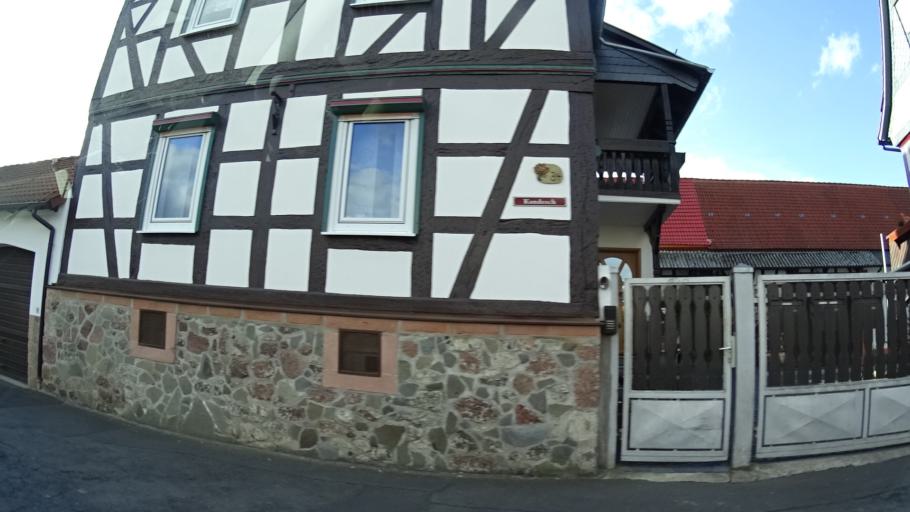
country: DE
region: Hesse
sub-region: Regierungsbezirk Darmstadt
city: Glauburg
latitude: 50.3154
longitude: 8.9995
